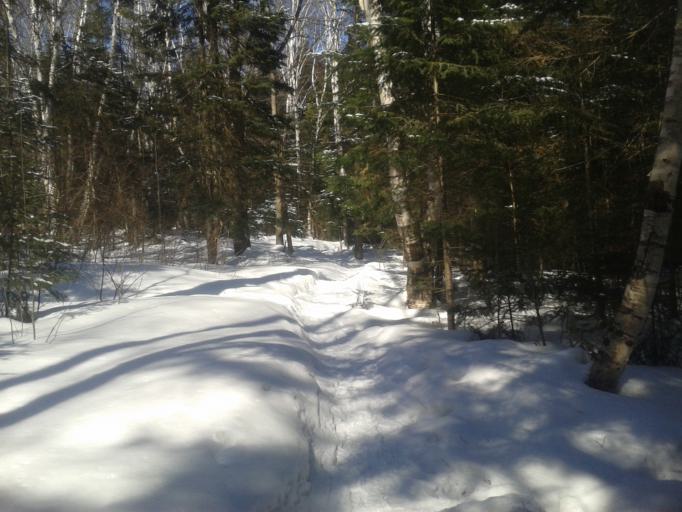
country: CA
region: Ontario
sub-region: Nipissing District
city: North Bay
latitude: 46.3433
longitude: -79.4957
